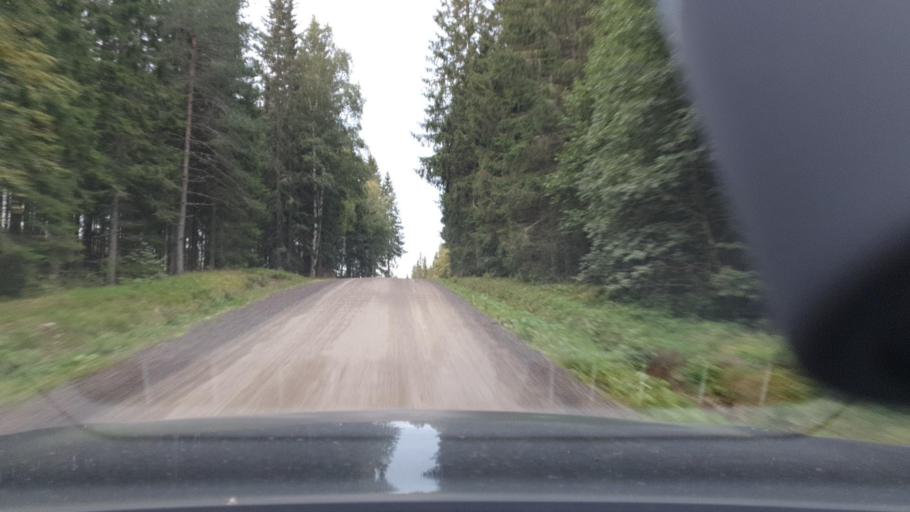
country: SE
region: Vaermland
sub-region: Sunne Kommun
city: Sunne
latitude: 59.8392
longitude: 12.9276
